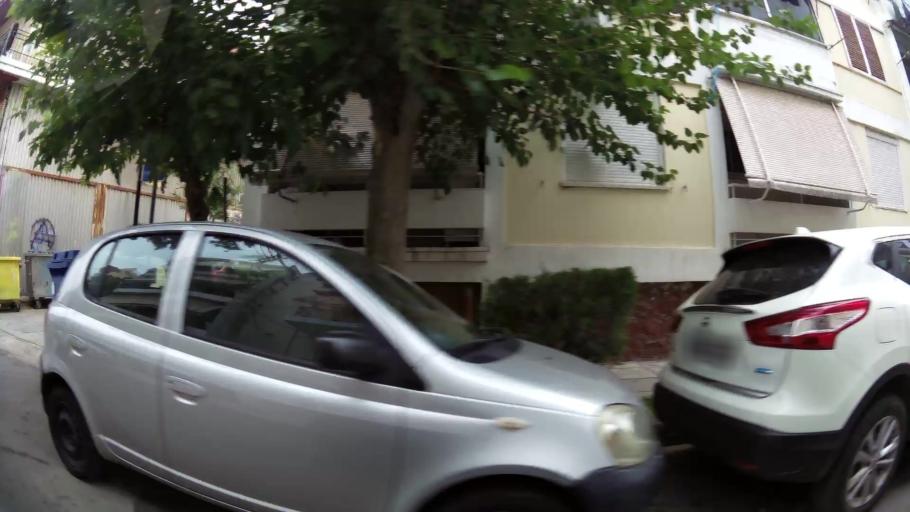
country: GR
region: Attica
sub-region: Nomarchia Athinas
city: Aigaleo
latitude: 37.9945
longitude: 23.6813
